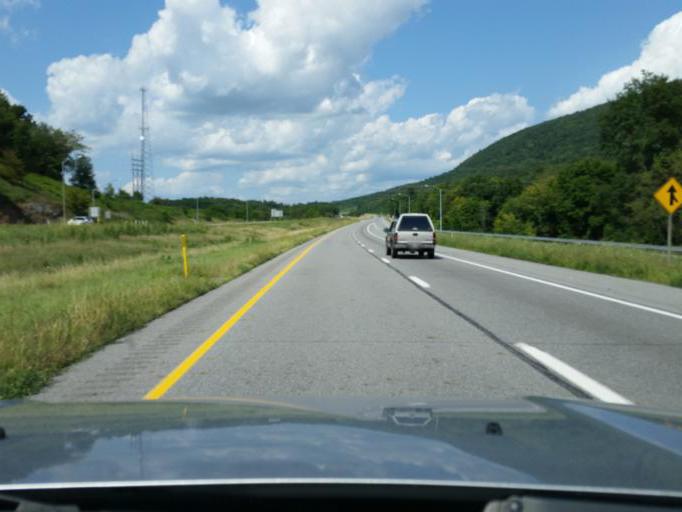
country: US
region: Pennsylvania
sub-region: Bedford County
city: Bedford
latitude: 40.1488
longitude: -78.5086
